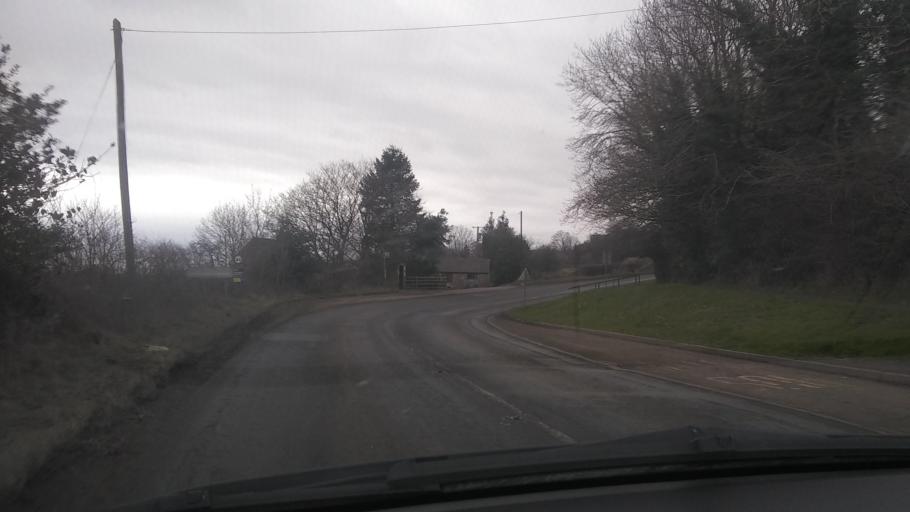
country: GB
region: England
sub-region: Shropshire
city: Cleobury Mortimer
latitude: 52.3862
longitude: -2.5594
